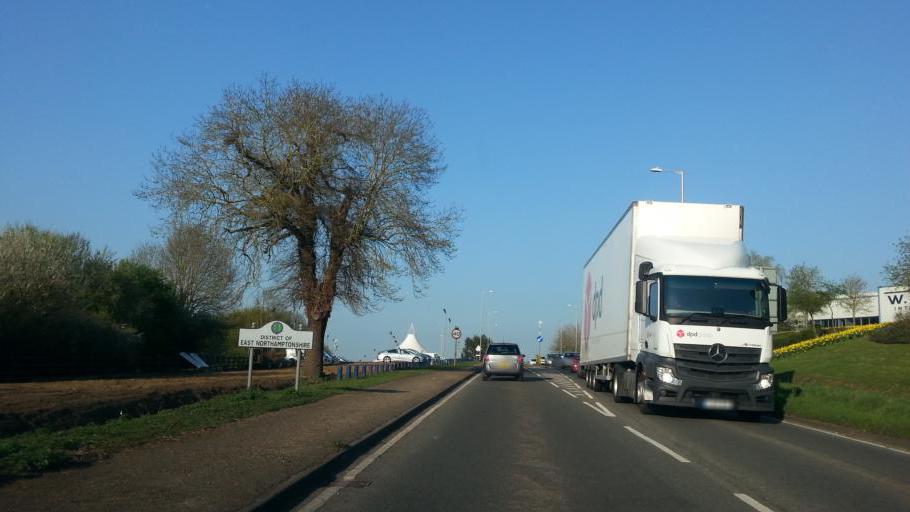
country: GB
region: England
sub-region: Northamptonshire
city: Irchester
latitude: 52.2954
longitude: -0.6338
